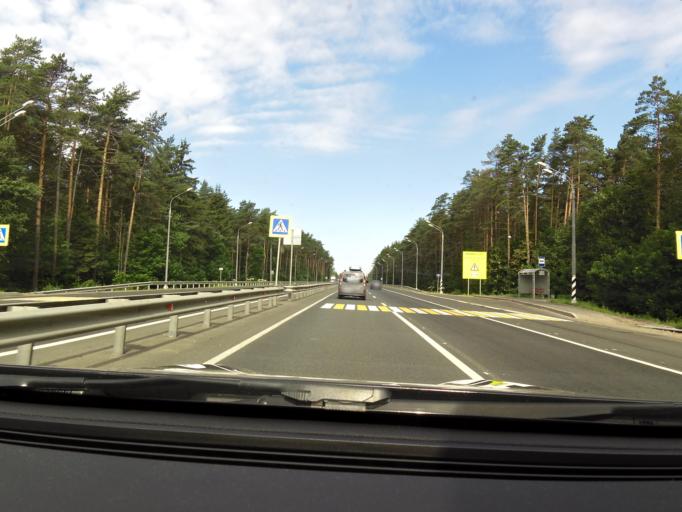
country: RU
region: Tverskaya
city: Emmaus
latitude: 56.7656
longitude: 36.1570
